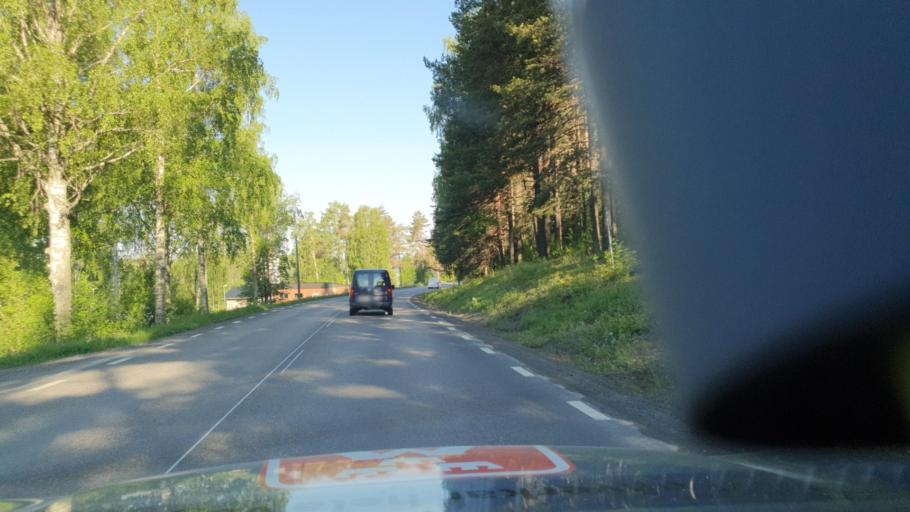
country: SE
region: Norrbotten
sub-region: Bodens Kommun
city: Boden
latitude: 65.8325
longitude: 21.6189
